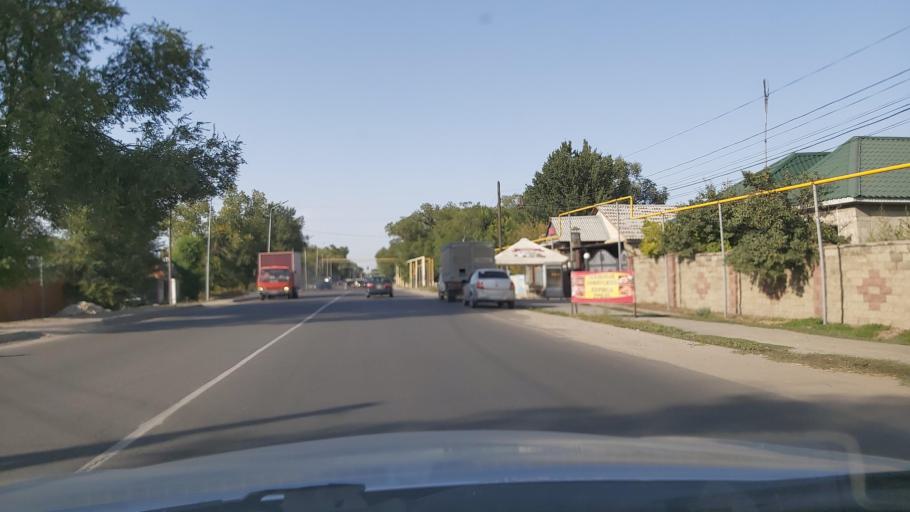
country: KZ
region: Almaty Oblysy
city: Energeticheskiy
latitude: 43.5010
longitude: 77.0419
